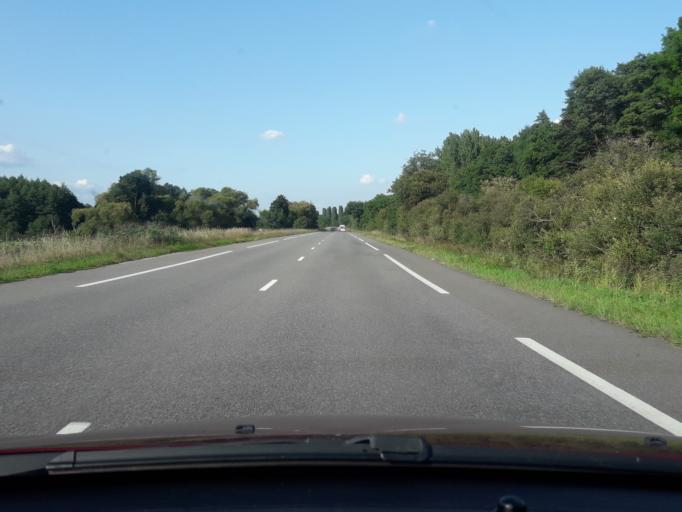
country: FR
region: Alsace
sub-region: Departement du Bas-Rhin
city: Betschdorf
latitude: 48.9417
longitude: 7.9506
